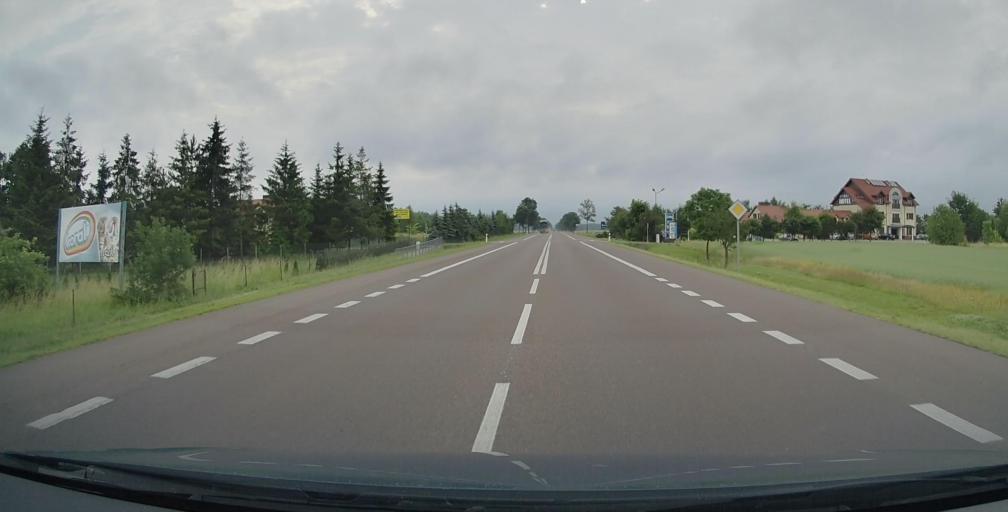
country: PL
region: Lublin Voivodeship
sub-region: Powiat bialski
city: Miedzyrzec Podlaski
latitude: 52.0292
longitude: 22.8848
